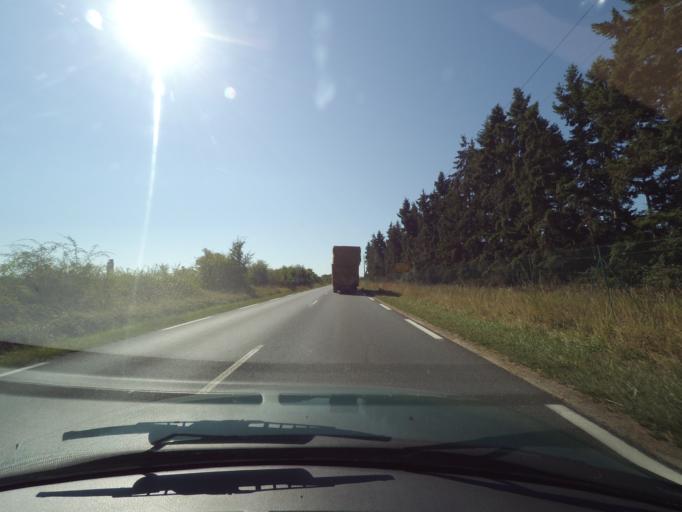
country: FR
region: Poitou-Charentes
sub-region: Departement de la Vienne
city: Lussac-les-Chateaux
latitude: 46.4103
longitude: 0.6897
